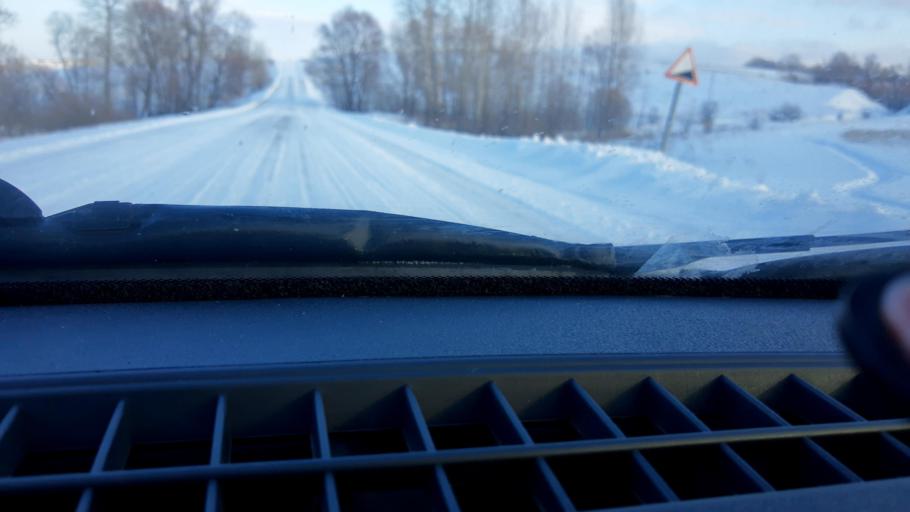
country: RU
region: Bashkortostan
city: Birsk
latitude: 55.1527
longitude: 55.6507
